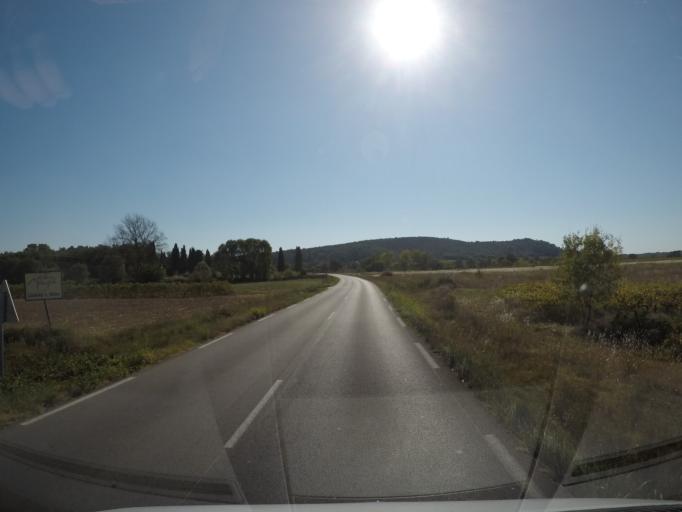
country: FR
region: Languedoc-Roussillon
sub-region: Departement du Gard
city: Ledignan
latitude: 44.0081
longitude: 4.1213
